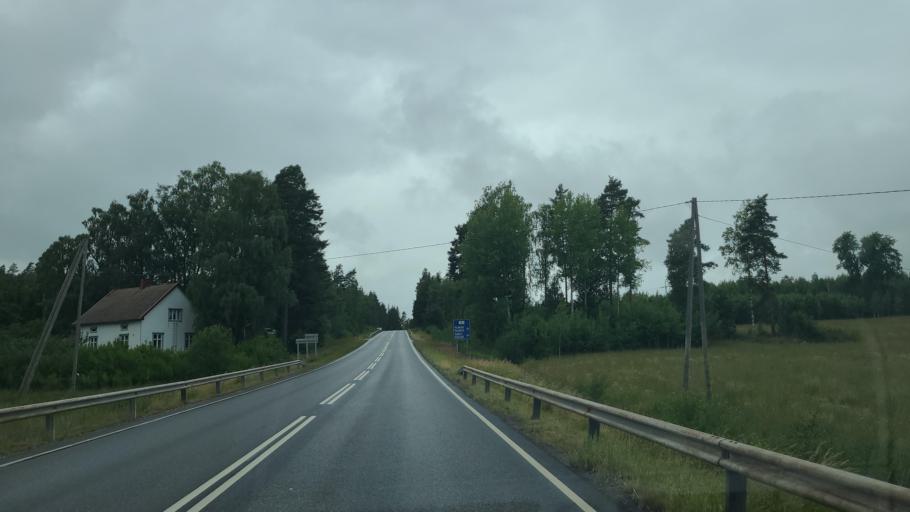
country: FI
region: Varsinais-Suomi
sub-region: Aboland-Turunmaa
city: Kimito
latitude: 60.2250
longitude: 22.6225
